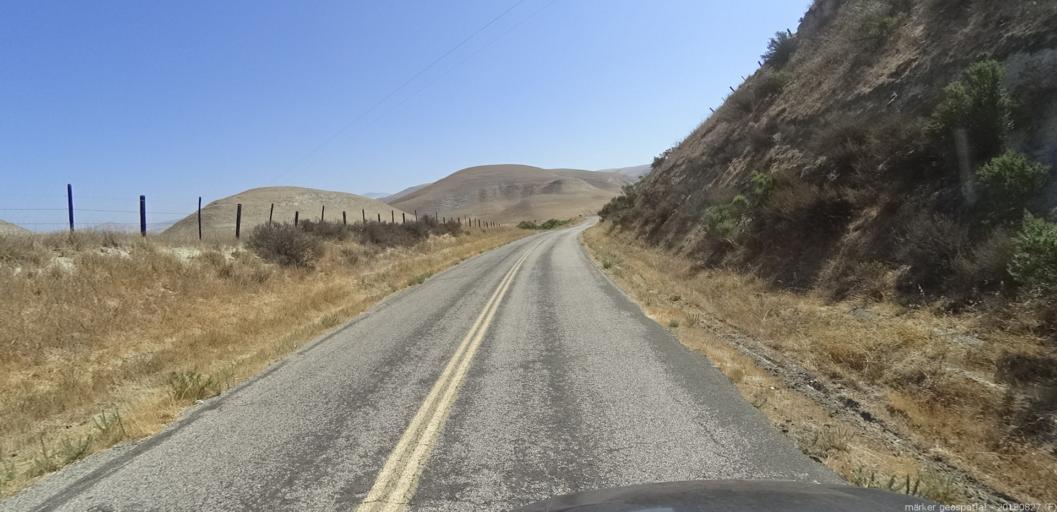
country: US
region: California
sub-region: Monterey County
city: King City
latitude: 36.2499
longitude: -121.0043
